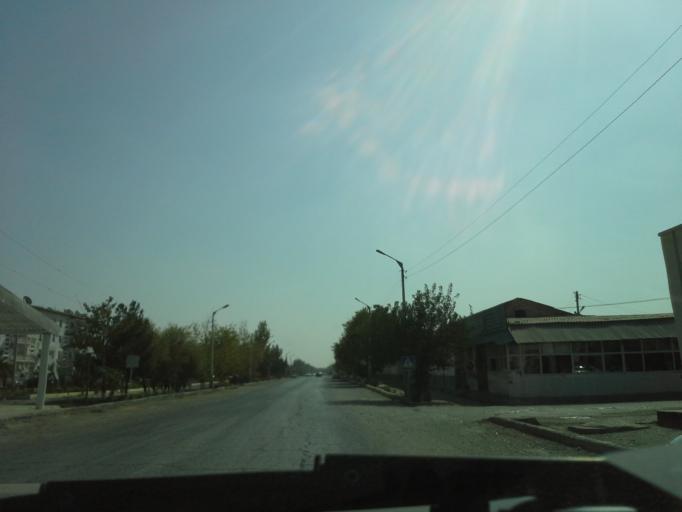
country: TM
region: Lebap
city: Atamyrat
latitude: 37.8419
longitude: 65.2028
